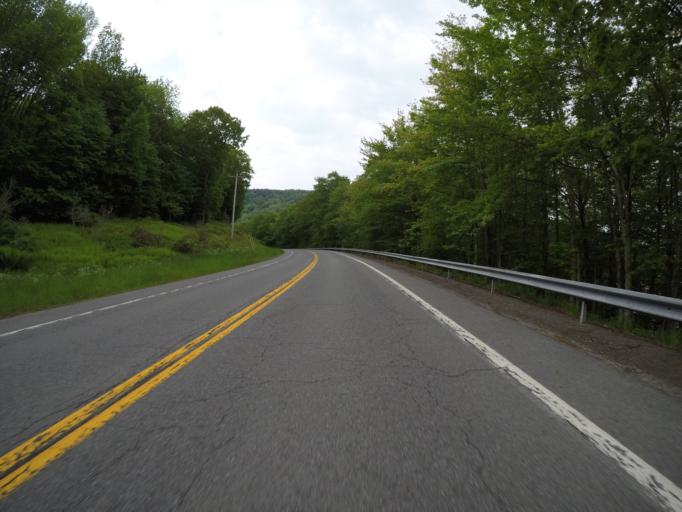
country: US
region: New York
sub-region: Sullivan County
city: Livingston Manor
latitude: 42.0770
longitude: -74.8348
